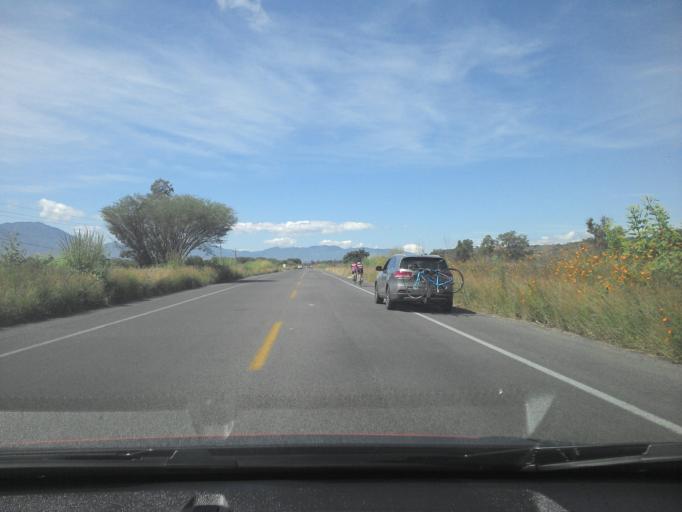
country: MX
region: Jalisco
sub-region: Teuchitlan
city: La Estanzuela
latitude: 20.6701
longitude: -103.8064
